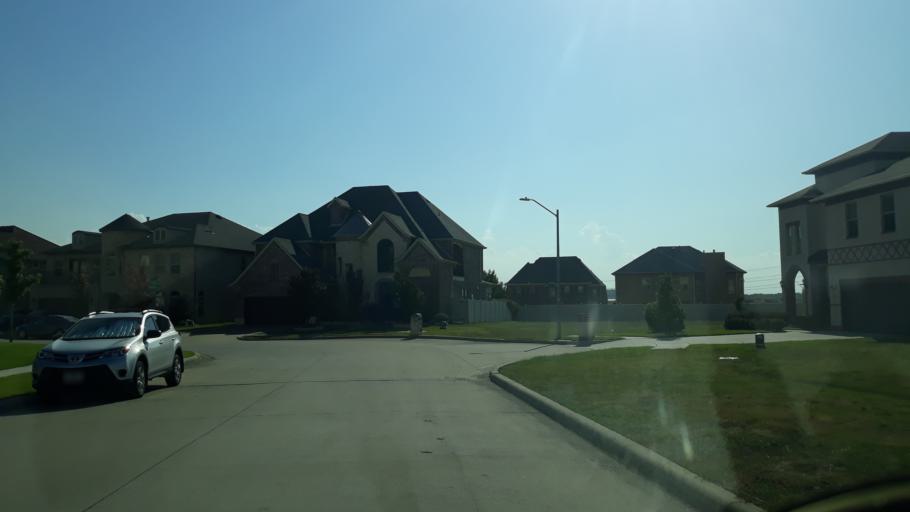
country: US
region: Texas
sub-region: Tarrant County
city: Euless
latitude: 32.8450
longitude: -97.0134
